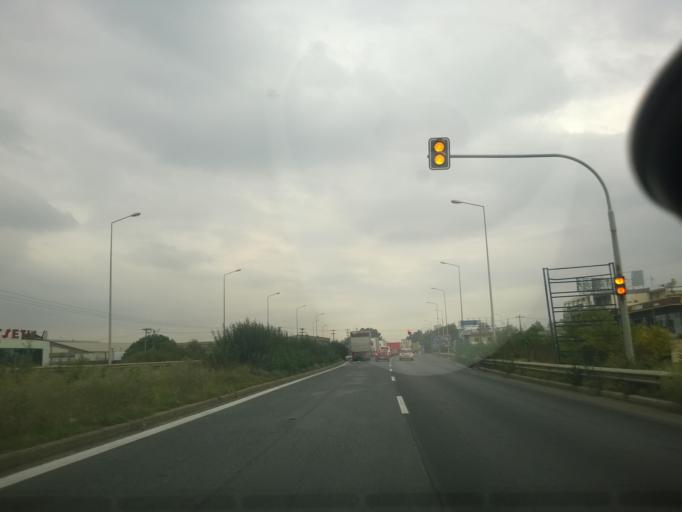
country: GR
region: Central Macedonia
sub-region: Nomos Thessalonikis
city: Nea Magnisia
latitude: 40.7012
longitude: 22.8227
